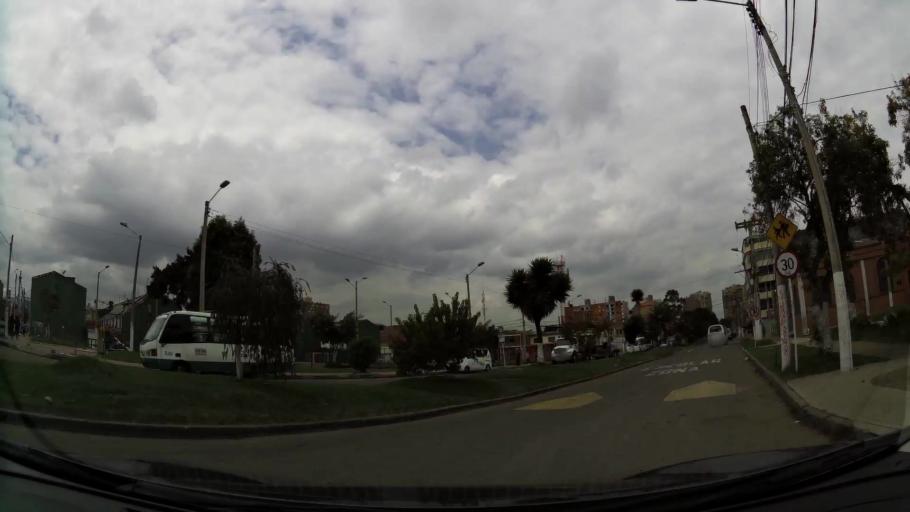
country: CO
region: Cundinamarca
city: La Calera
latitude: 4.7679
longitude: -74.0289
